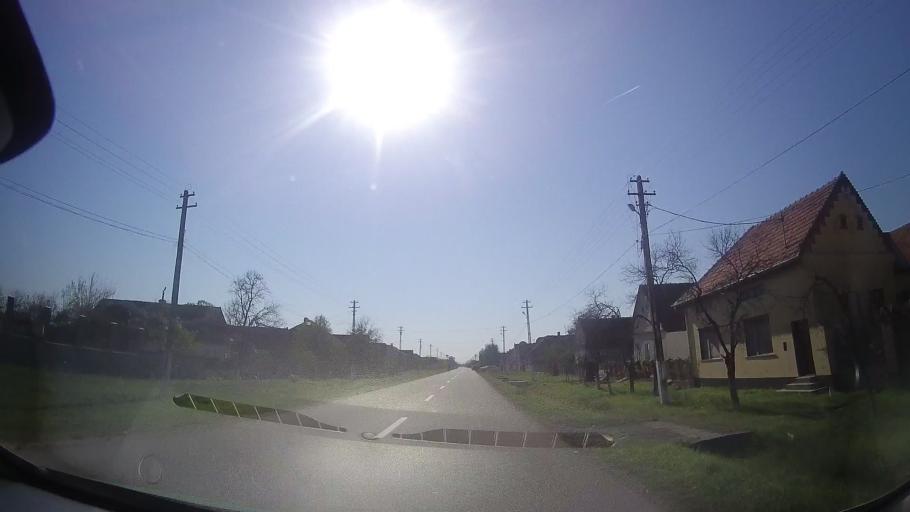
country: RO
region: Timis
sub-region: Comuna Ghizela
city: Ghizela
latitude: 45.7997
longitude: 21.7254
